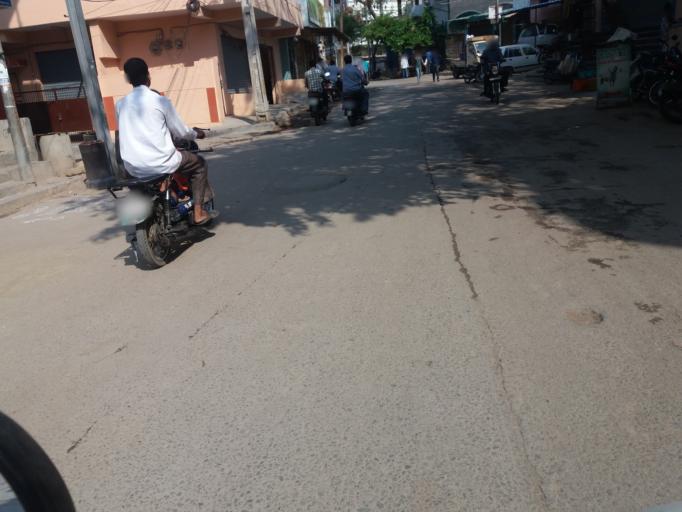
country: IN
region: Telangana
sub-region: Hyderabad
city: Malkajgiri
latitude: 17.4148
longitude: 78.5119
